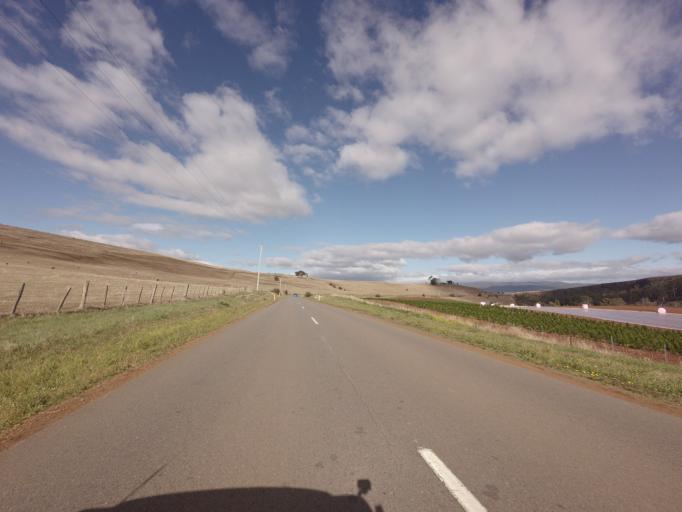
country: AU
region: Tasmania
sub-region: Derwent Valley
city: New Norfolk
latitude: -42.6957
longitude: 146.9324
